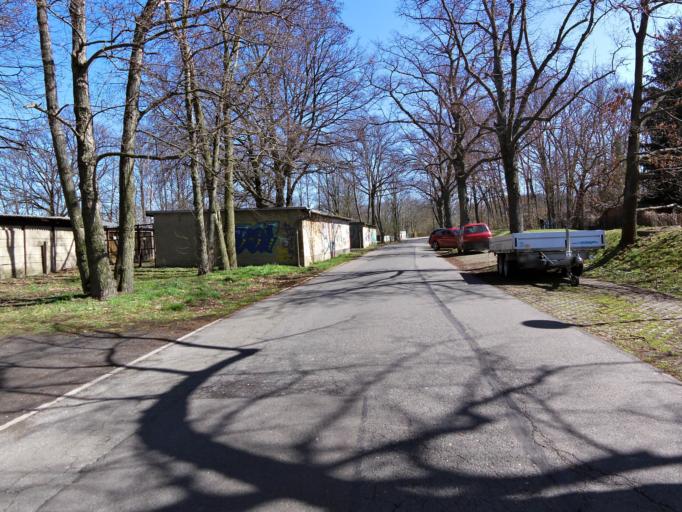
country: DE
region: Saxony
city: Markkleeberg
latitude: 51.2786
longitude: 12.3787
